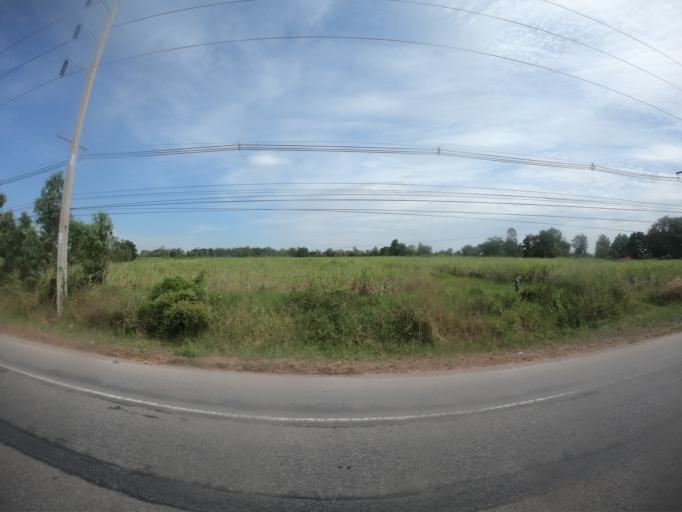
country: TH
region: Maha Sarakham
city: Chiang Yuen
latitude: 16.4259
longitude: 103.0674
